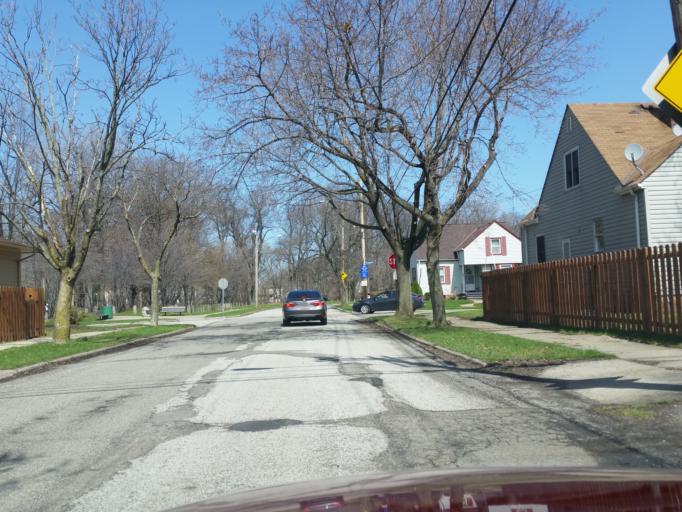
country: US
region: Ohio
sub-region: Cuyahoga County
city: Brooklyn Heights
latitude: 41.4379
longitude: -81.6913
